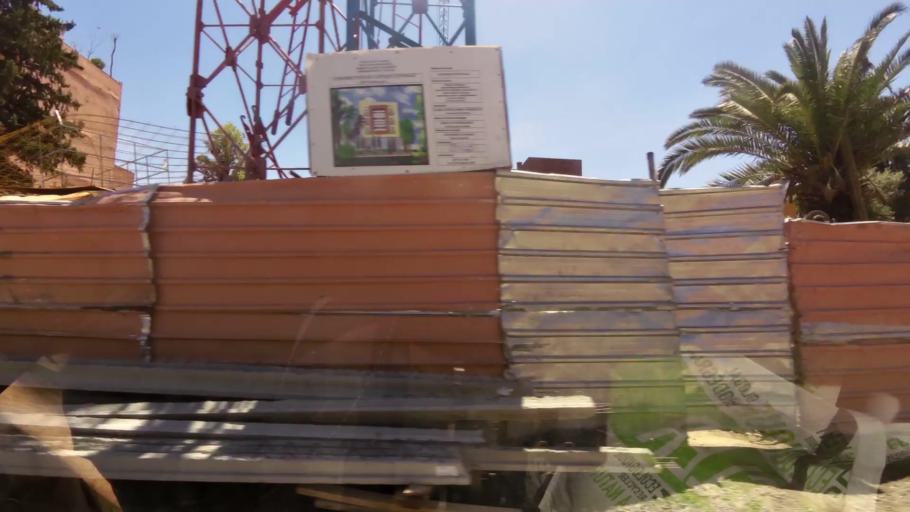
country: MA
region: Marrakech-Tensift-Al Haouz
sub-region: Marrakech
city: Marrakesh
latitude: 31.6265
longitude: -8.0187
